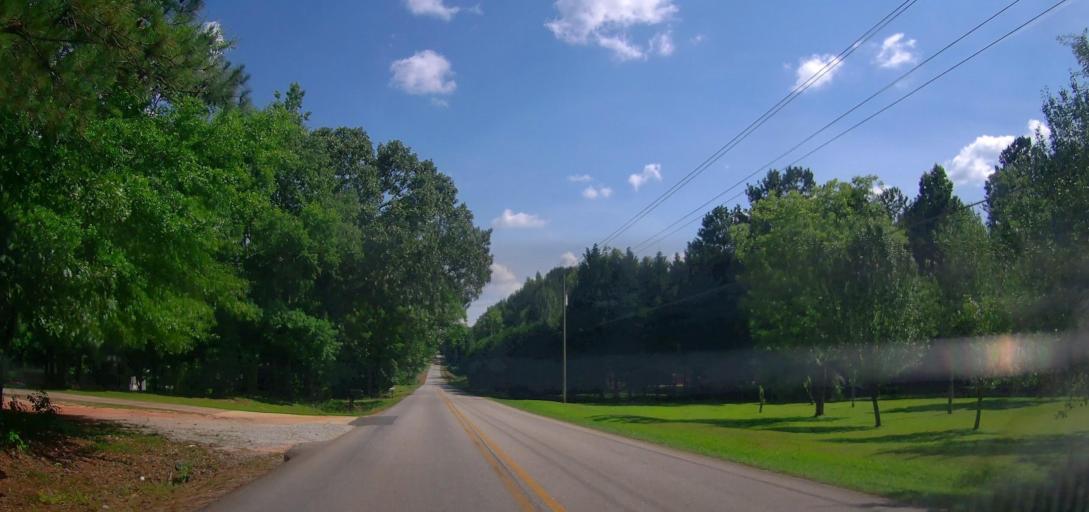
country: US
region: Georgia
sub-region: Spalding County
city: East Griffin
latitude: 33.2699
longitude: -84.1901
